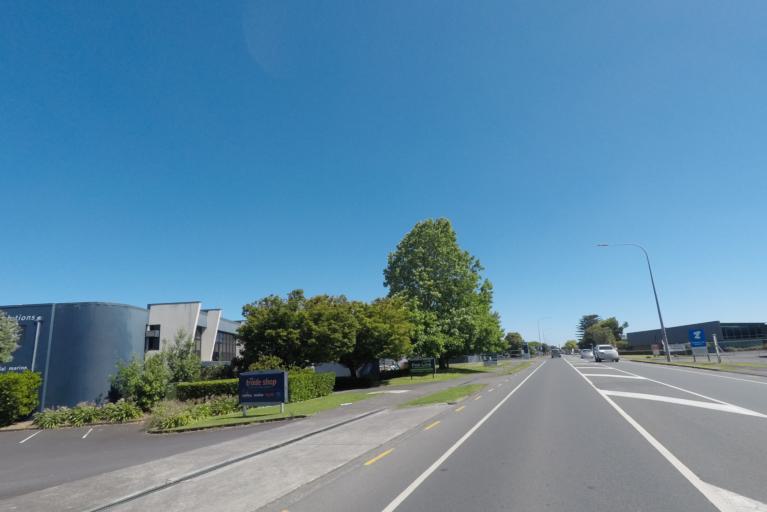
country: NZ
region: Auckland
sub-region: Auckland
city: Rosebank
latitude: -36.8769
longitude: 174.6699
